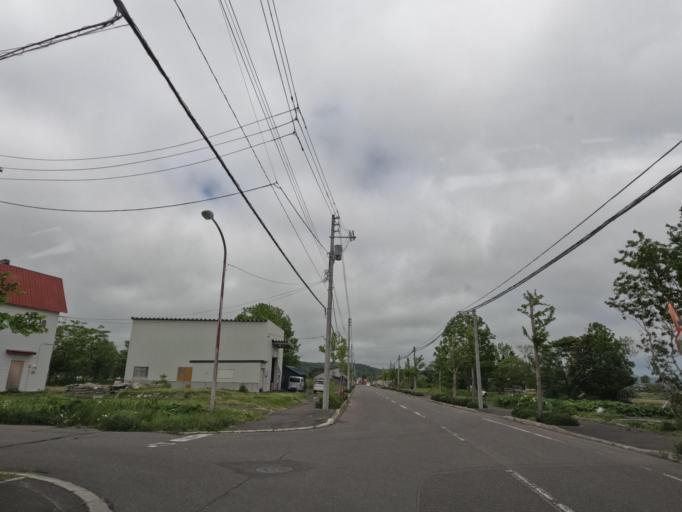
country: JP
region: Hokkaido
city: Tobetsu
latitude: 43.2338
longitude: 141.5151
